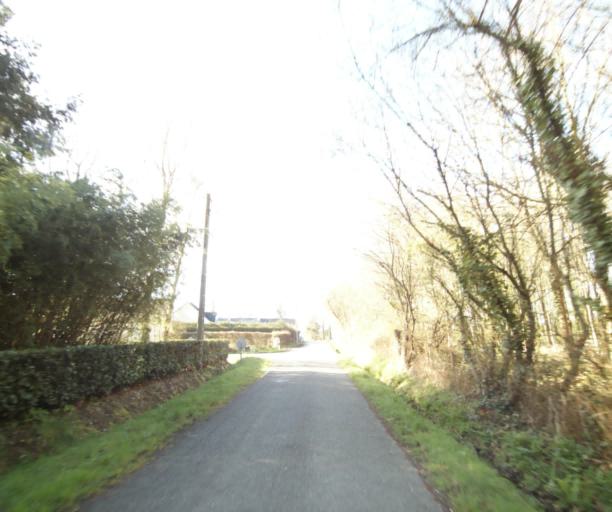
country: FR
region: Pays de la Loire
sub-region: Departement de la Loire-Atlantique
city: Bouvron
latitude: 47.4050
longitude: -1.8485
